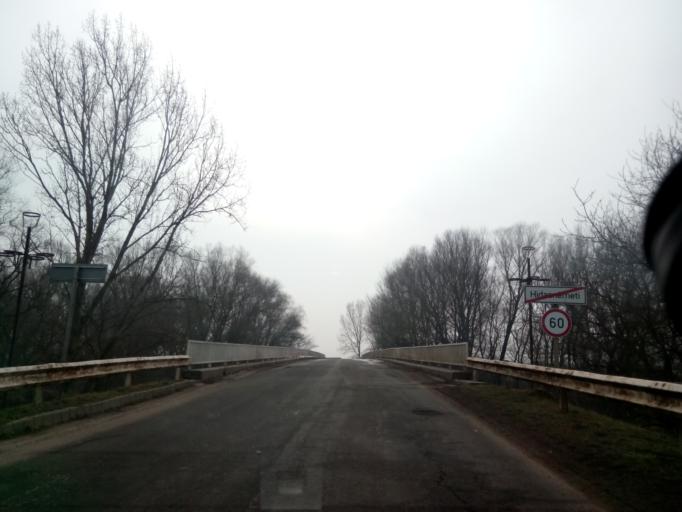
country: HU
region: Borsod-Abauj-Zemplen
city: Gonc
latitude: 48.4984
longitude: 21.2300
